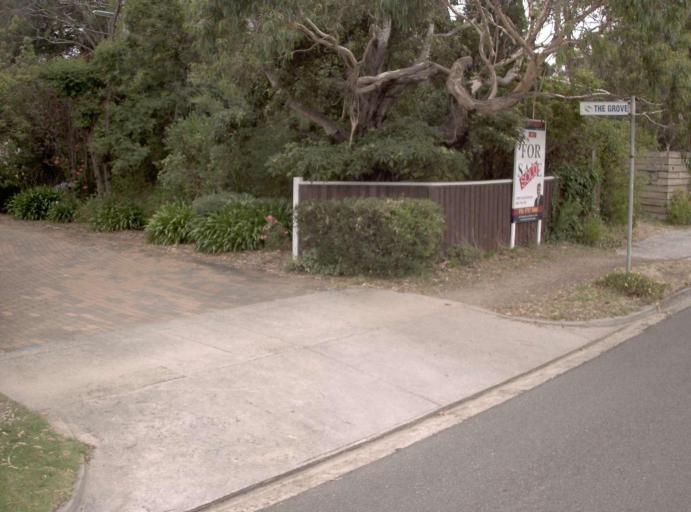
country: AU
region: Victoria
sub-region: Frankston
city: Frankston
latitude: -38.1588
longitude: 145.1047
